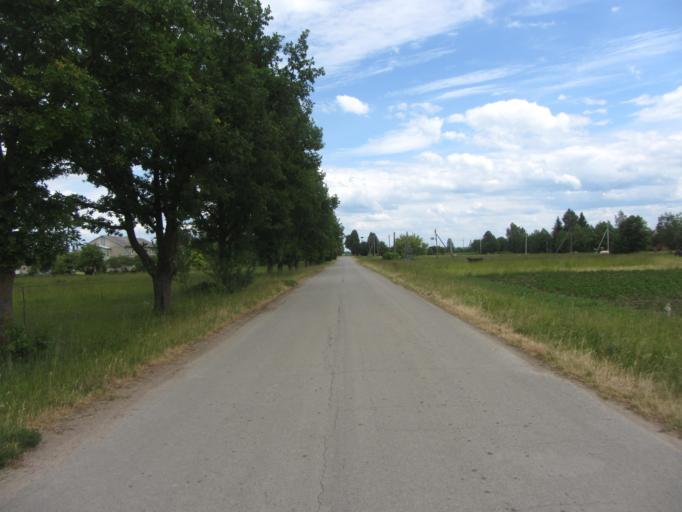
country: LT
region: Panevezys
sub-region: Birzai
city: Birzai
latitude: 56.4128
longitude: 24.8862
